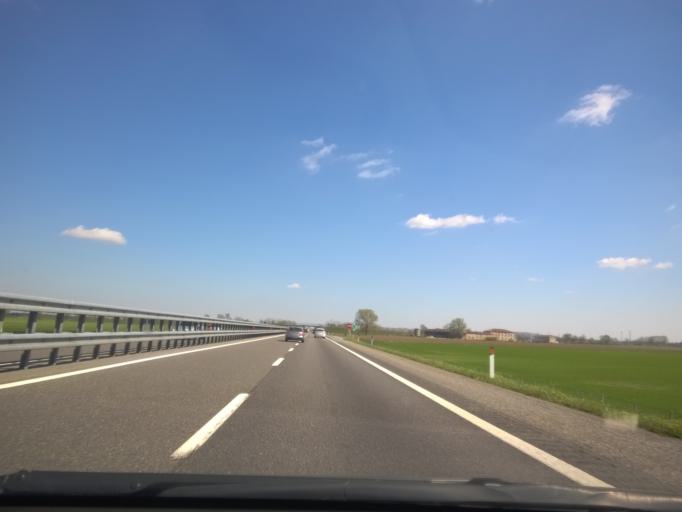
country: IT
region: Emilia-Romagna
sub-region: Provincia di Piacenza
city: Sarmato
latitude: 45.0711
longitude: 9.4875
